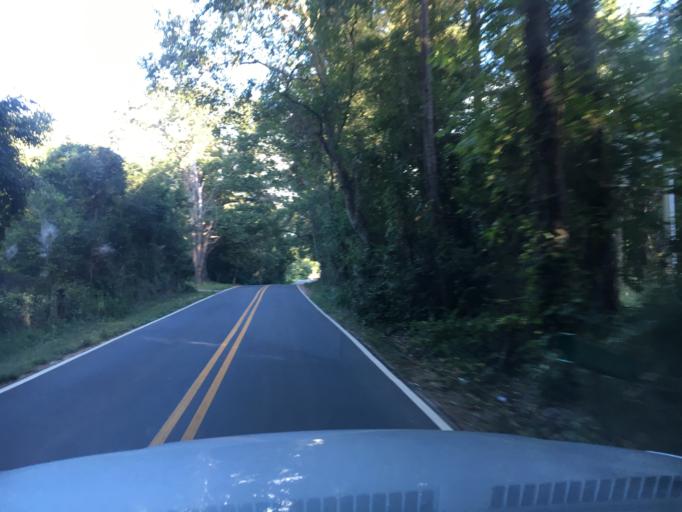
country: US
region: South Carolina
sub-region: Spartanburg County
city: Roebuck
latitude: 34.8927
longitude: -82.0281
